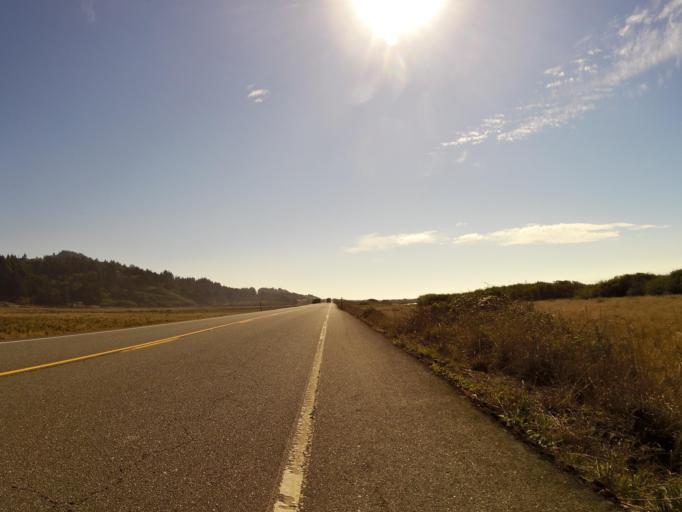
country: US
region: Oregon
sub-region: Curry County
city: Gold Beach
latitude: 42.5614
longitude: -124.3862
